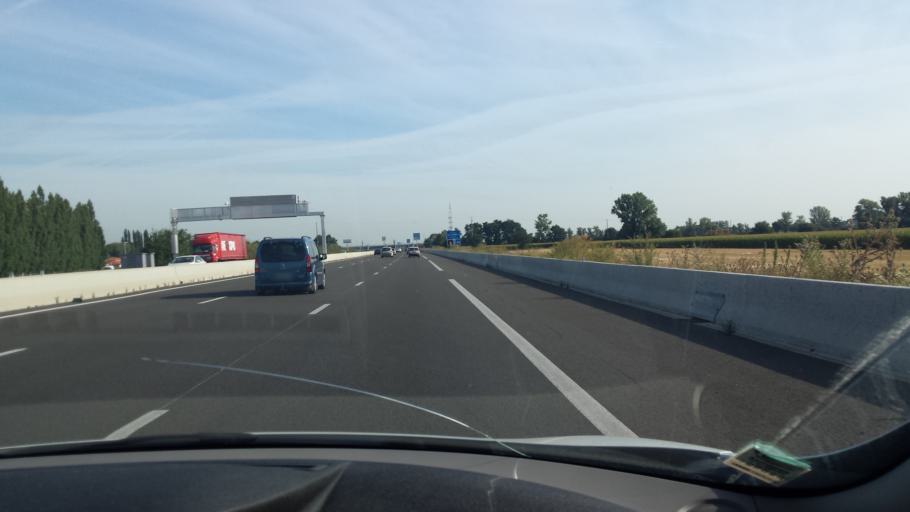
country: FR
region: Auvergne
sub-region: Departement du Puy-de-Dome
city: Gerzat
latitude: 45.8308
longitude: 3.1591
